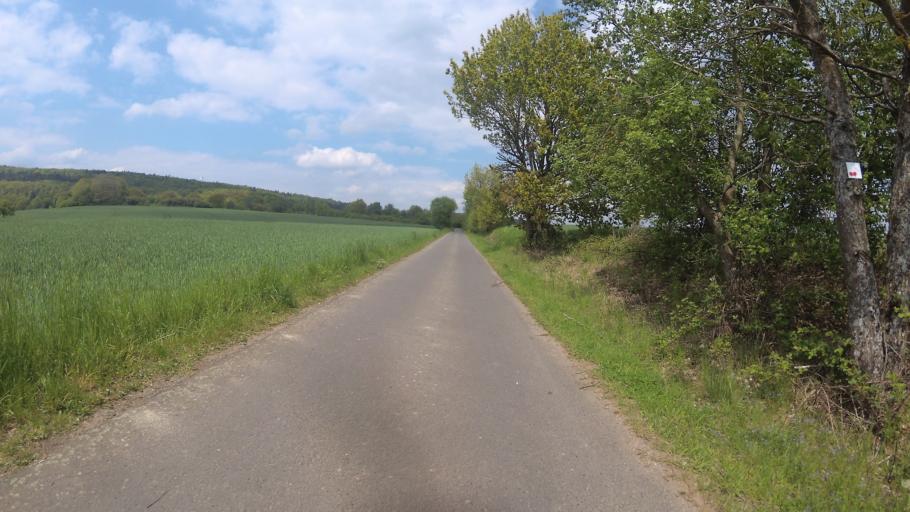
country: DE
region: Rheinland-Pfalz
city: Frohnhofen
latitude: 49.4569
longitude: 7.3099
